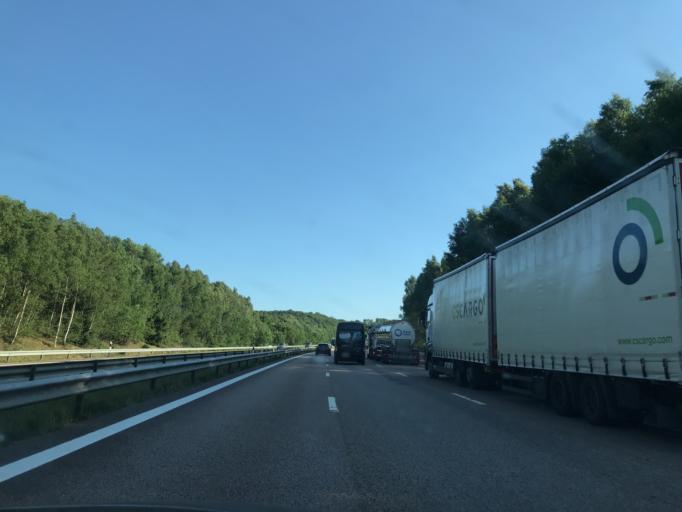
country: SE
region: Skane
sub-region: Bastads Kommun
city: Forslov
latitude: 56.3350
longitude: 12.9148
